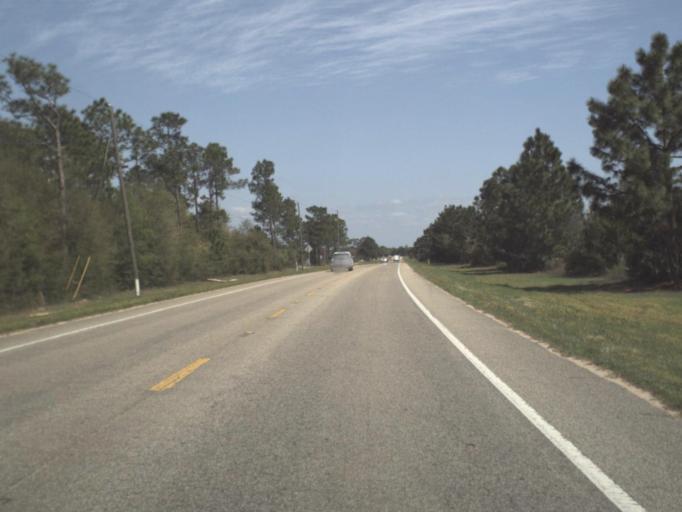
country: US
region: Florida
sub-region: Okaloosa County
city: Crestview
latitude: 30.7503
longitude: -86.4274
